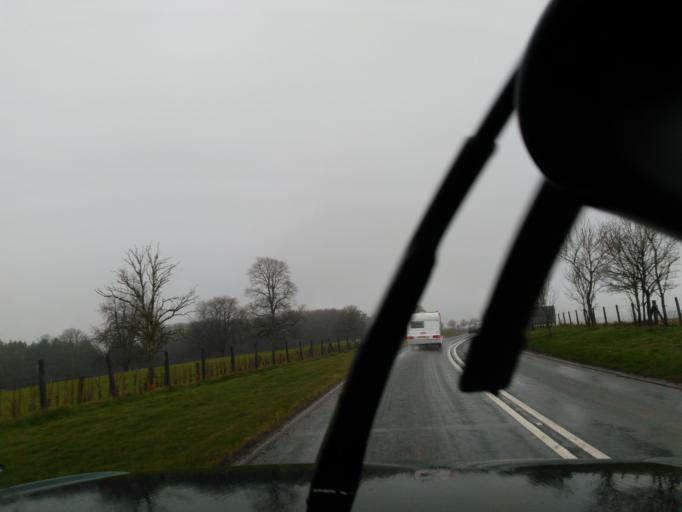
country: GB
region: England
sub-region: Somerset
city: Frome
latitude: 51.2090
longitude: -2.3441
